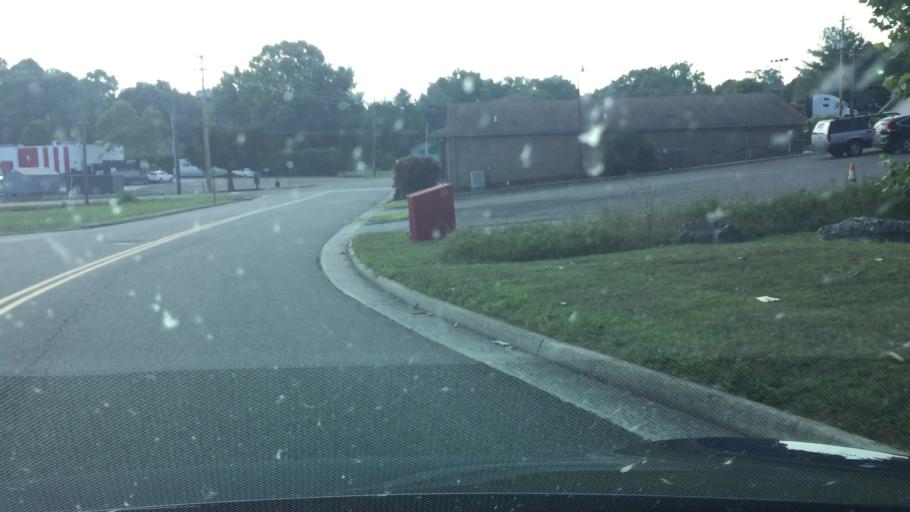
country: US
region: Virginia
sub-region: Pulaski County
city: Pulaski
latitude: 37.0529
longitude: -80.7493
